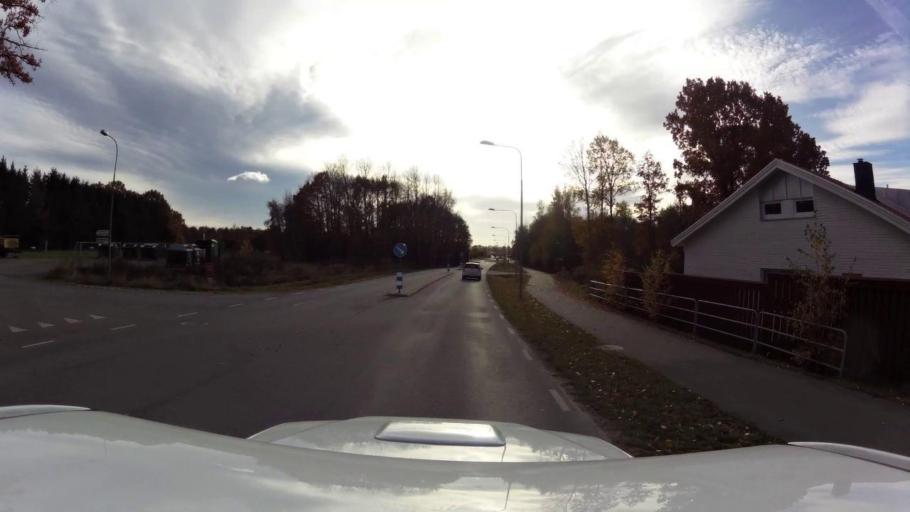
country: SE
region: OEstergoetland
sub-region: Linkopings Kommun
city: Ekangen
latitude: 58.4625
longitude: 15.6403
